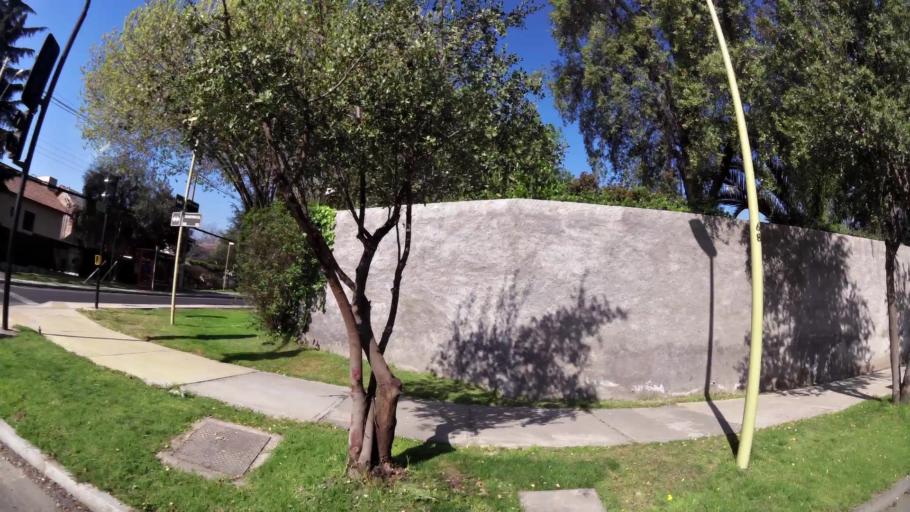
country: CL
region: Santiago Metropolitan
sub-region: Provincia de Santiago
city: Villa Presidente Frei, Nunoa, Santiago, Chile
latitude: -33.4010
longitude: -70.5290
